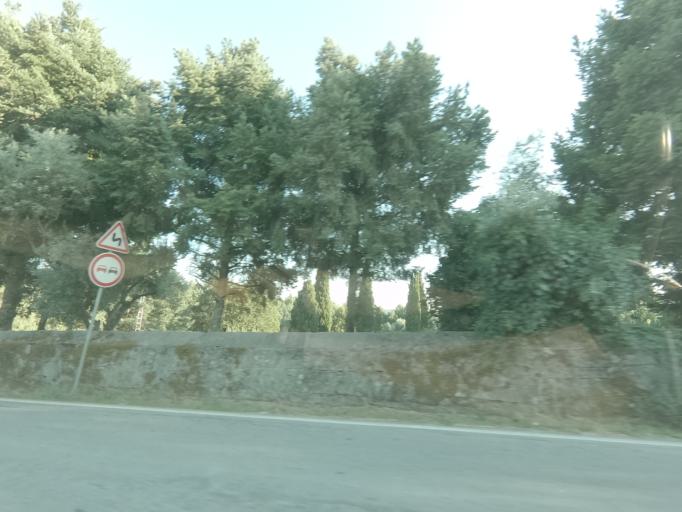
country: PT
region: Vila Real
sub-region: Vila Real
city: Vila Real
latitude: 41.2969
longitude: -7.7106
